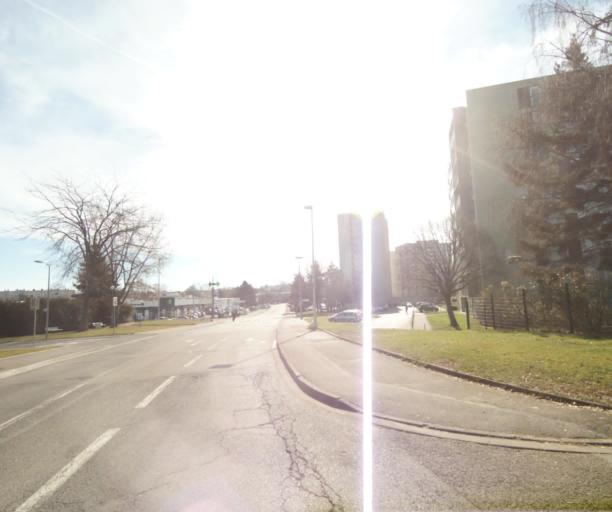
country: FR
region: Lorraine
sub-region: Departement de Meurthe-et-Moselle
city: Vandoeuvre-les-Nancy
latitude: 48.6664
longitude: 6.1818
